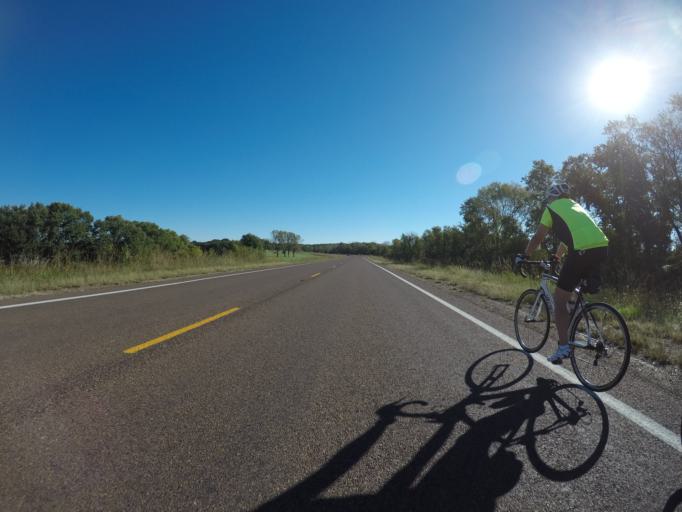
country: US
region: Kansas
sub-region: Johnson County
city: De Soto
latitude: 39.0067
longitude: -95.0244
